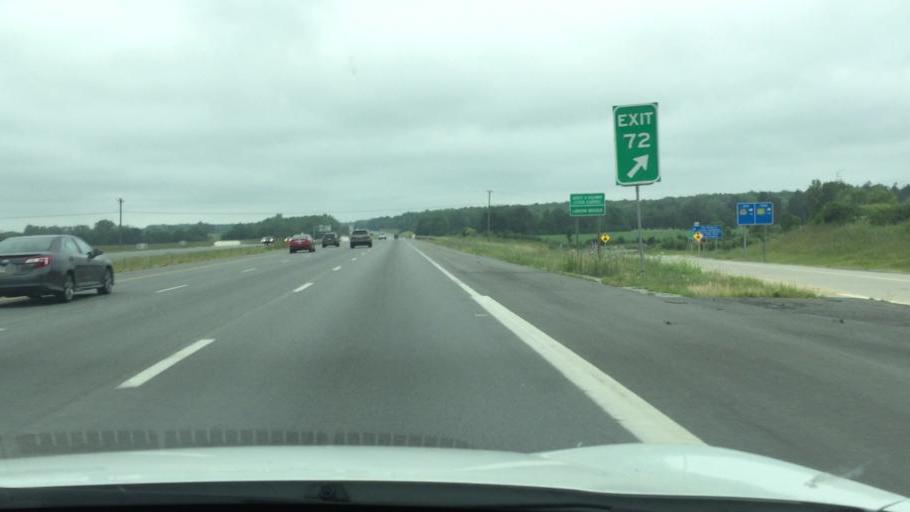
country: US
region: Ohio
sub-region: Madison County
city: Choctaw Lake
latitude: 39.9429
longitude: -83.4968
